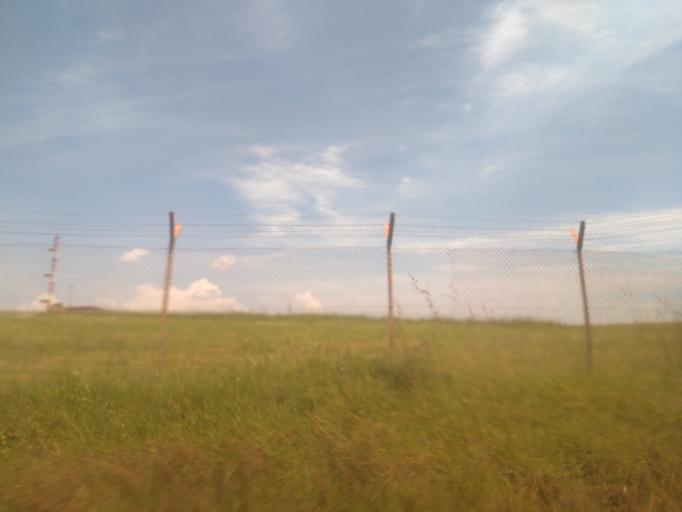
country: UG
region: Central Region
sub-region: Wakiso District
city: Entebbe
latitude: 0.0520
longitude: 32.4349
